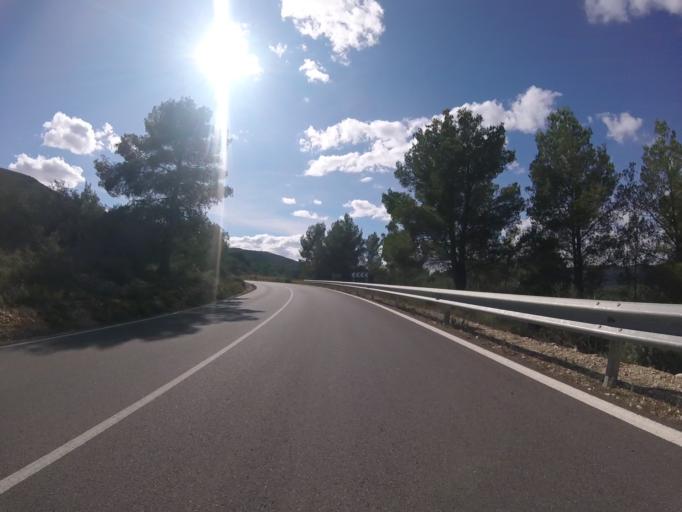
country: ES
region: Valencia
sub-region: Provincia de Castello
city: Cati
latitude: 40.4347
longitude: 0.0966
